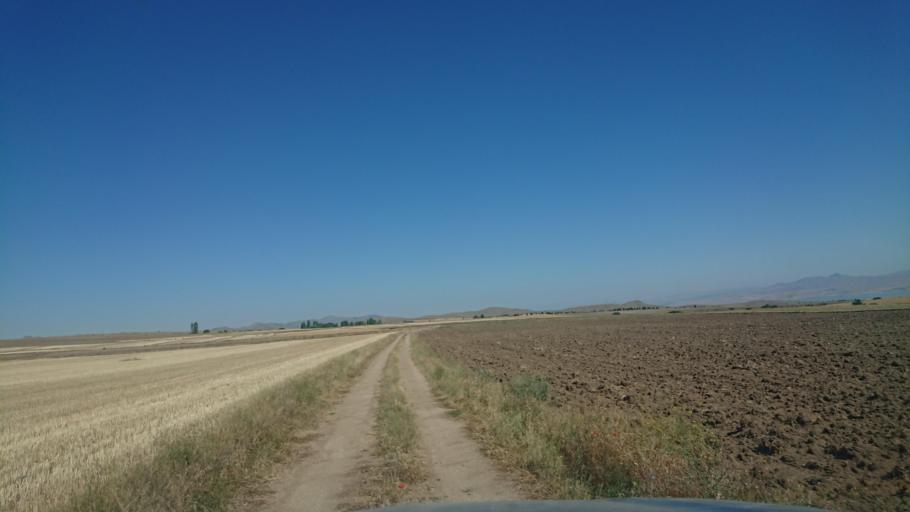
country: TR
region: Aksaray
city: Sariyahsi
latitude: 38.9353
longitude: 33.8418
